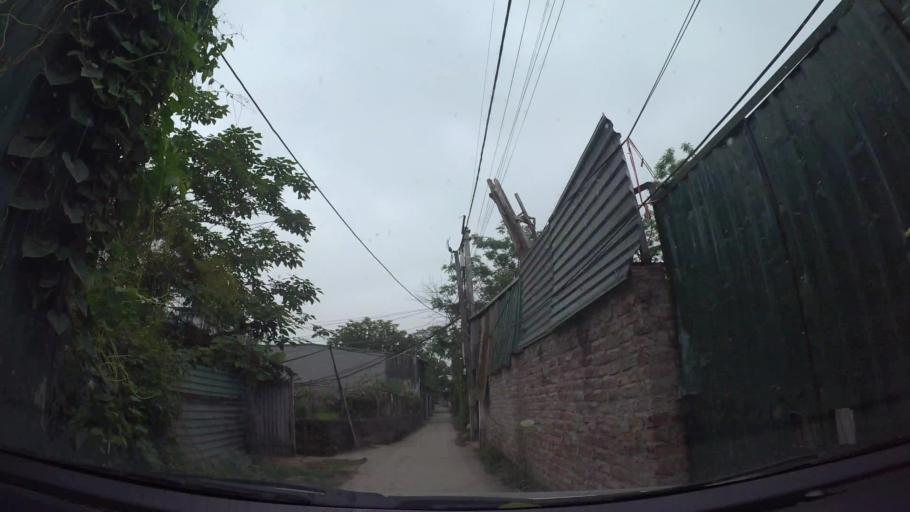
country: VN
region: Ha Noi
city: Tay Ho
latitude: 21.0700
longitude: 105.8276
